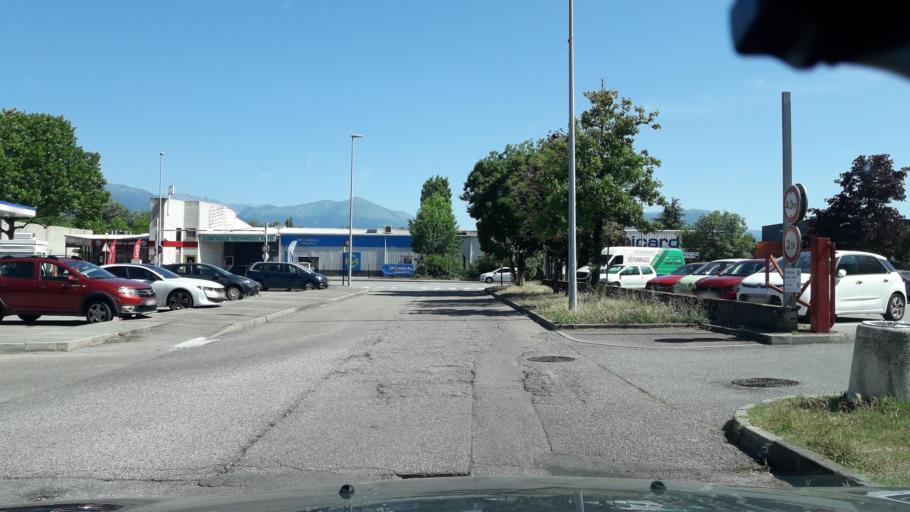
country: FR
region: Rhone-Alpes
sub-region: Departement de l'Isere
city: Seyssins
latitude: 45.1482
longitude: 5.6920
